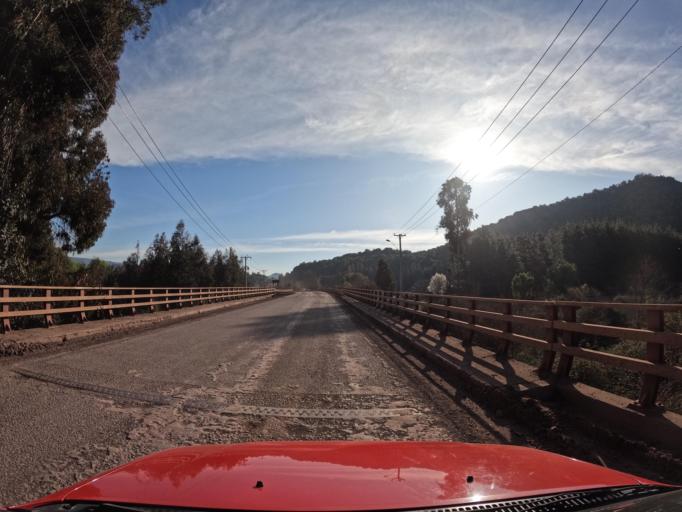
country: CL
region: Maule
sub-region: Provincia de Curico
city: Teno
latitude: -34.9684
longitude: -70.9432
